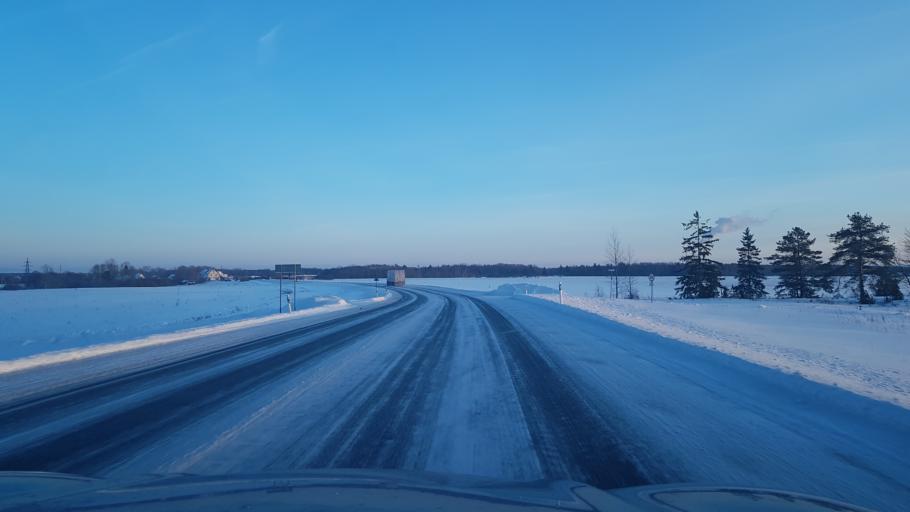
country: EE
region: Ida-Virumaa
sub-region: Narva-Joesuu linn
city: Narva-Joesuu
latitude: 59.4035
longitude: 28.0526
